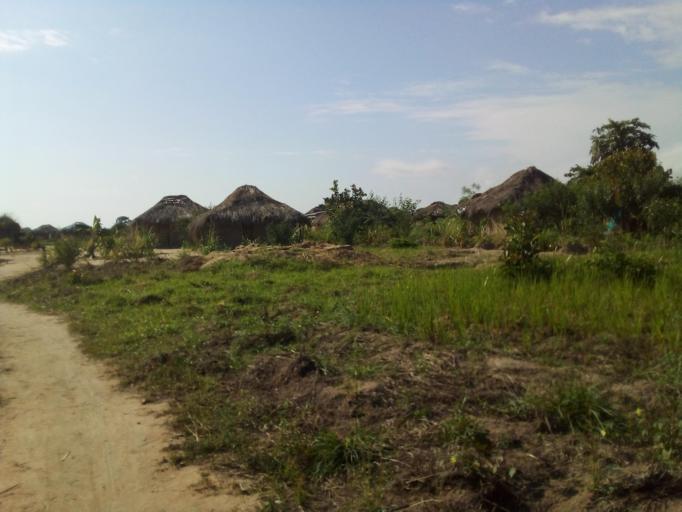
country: MZ
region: Zambezia
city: Quelimane
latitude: -17.5535
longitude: 36.7032
